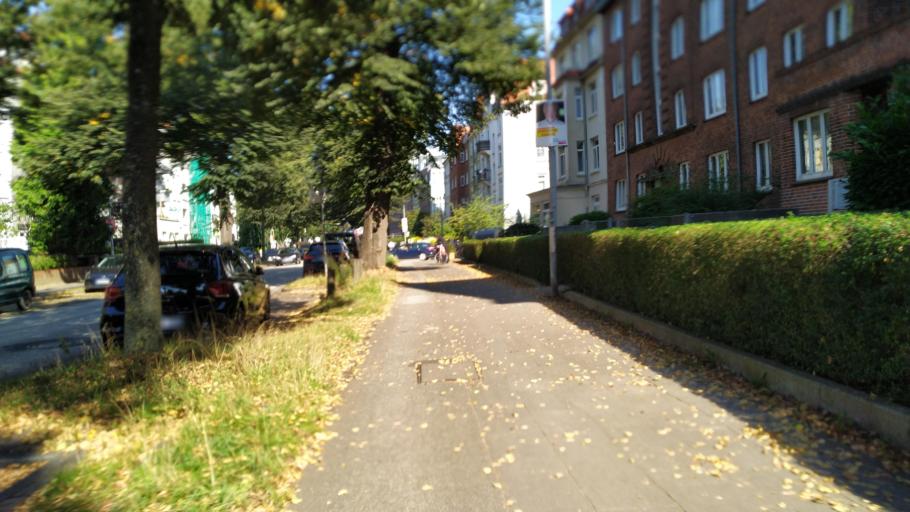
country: DE
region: Schleswig-Holstein
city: Luebeck
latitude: 53.8543
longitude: 10.6655
